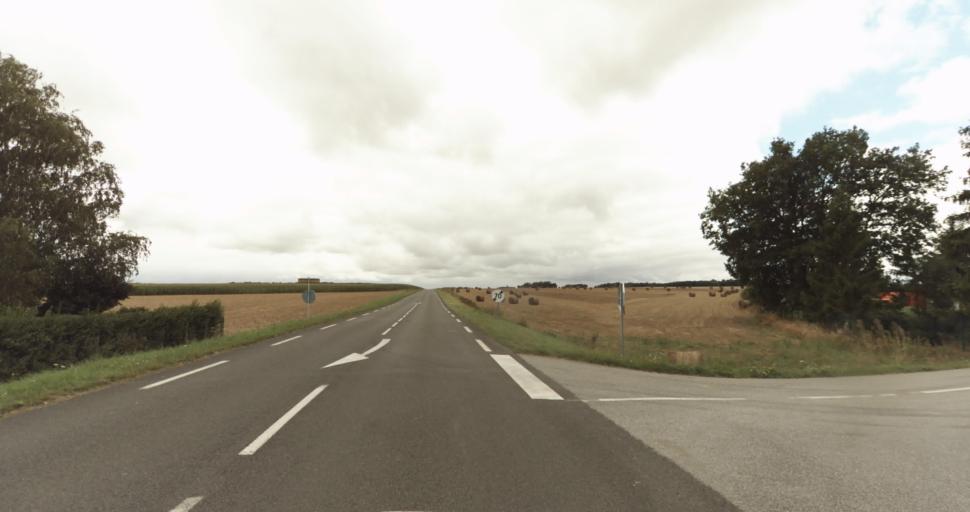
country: FR
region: Haute-Normandie
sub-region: Departement de l'Eure
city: Evreux
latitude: 48.9524
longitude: 1.1624
